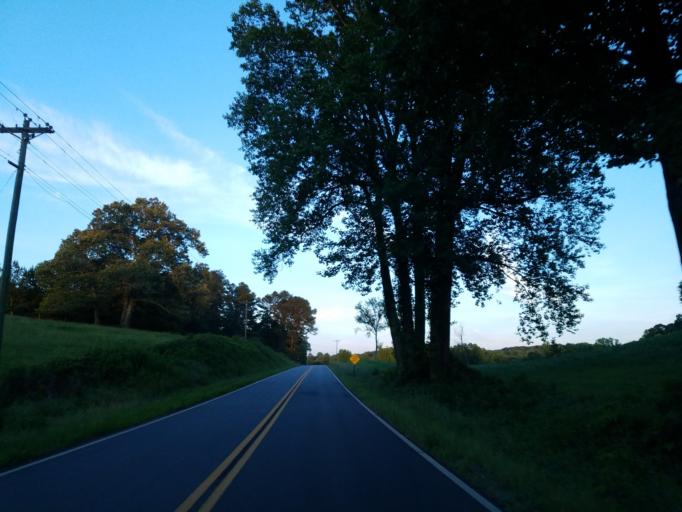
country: US
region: Georgia
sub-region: Lumpkin County
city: Dahlonega
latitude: 34.5647
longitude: -83.9556
